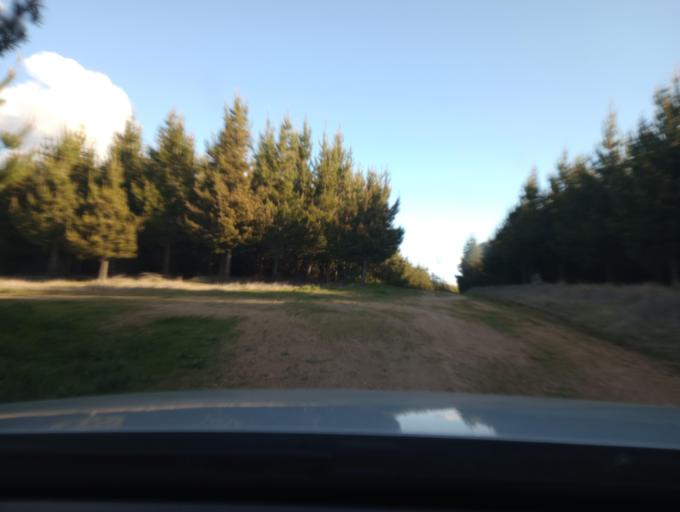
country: AU
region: New South Wales
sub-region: Blayney
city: Millthorpe
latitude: -33.4029
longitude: 149.3118
